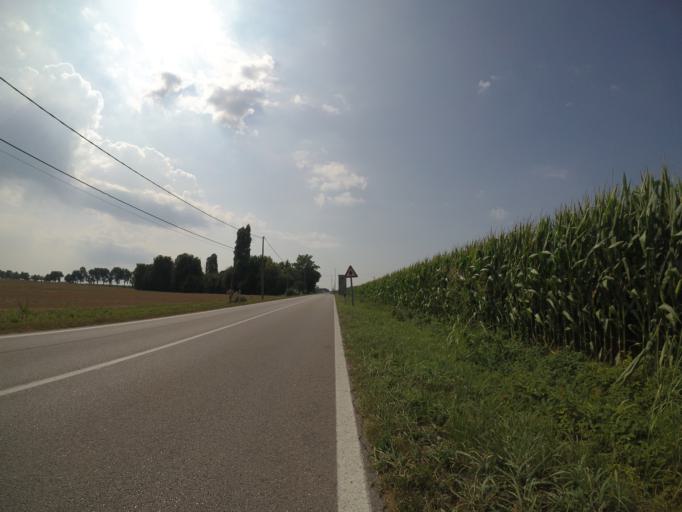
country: IT
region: Friuli Venezia Giulia
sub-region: Provincia di Udine
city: Pertegada
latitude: 45.7568
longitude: 13.0573
